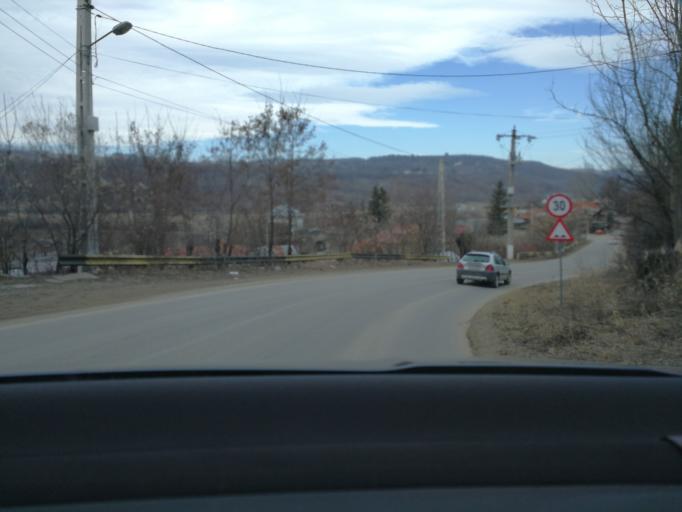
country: RO
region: Prahova
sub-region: Comuna Telega
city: Telega
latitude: 45.1401
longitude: 25.7736
